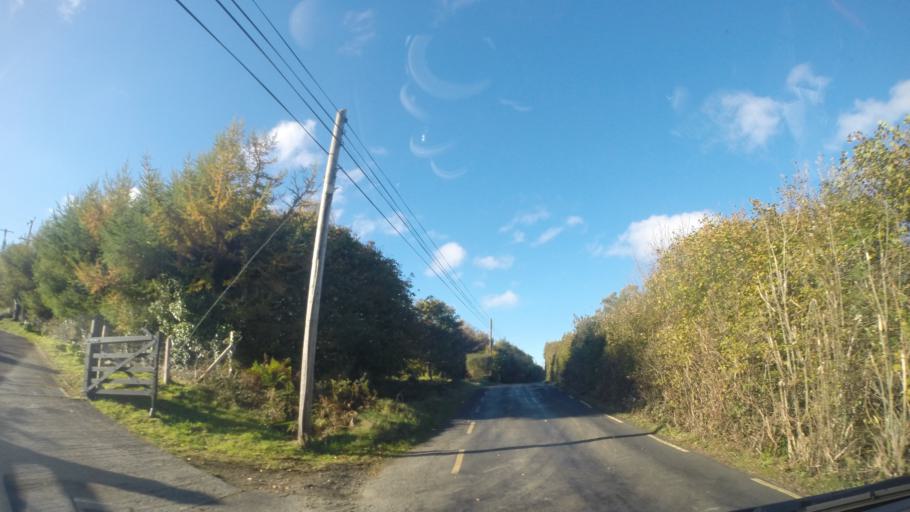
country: IE
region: Ulster
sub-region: County Donegal
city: Dungloe
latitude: 54.8374
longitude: -8.3883
